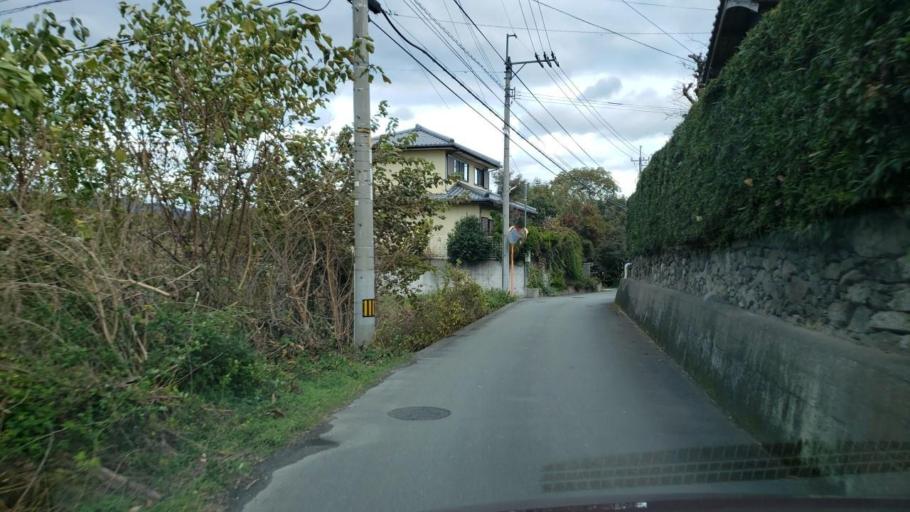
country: JP
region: Tokushima
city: Wakimachi
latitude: 34.0569
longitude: 134.1526
